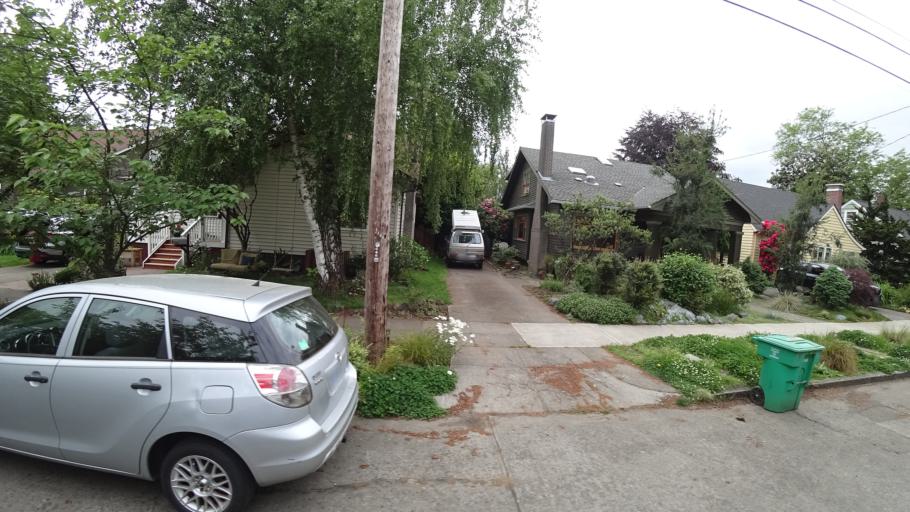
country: US
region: Oregon
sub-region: Multnomah County
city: Lents
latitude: 45.5106
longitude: -122.6066
